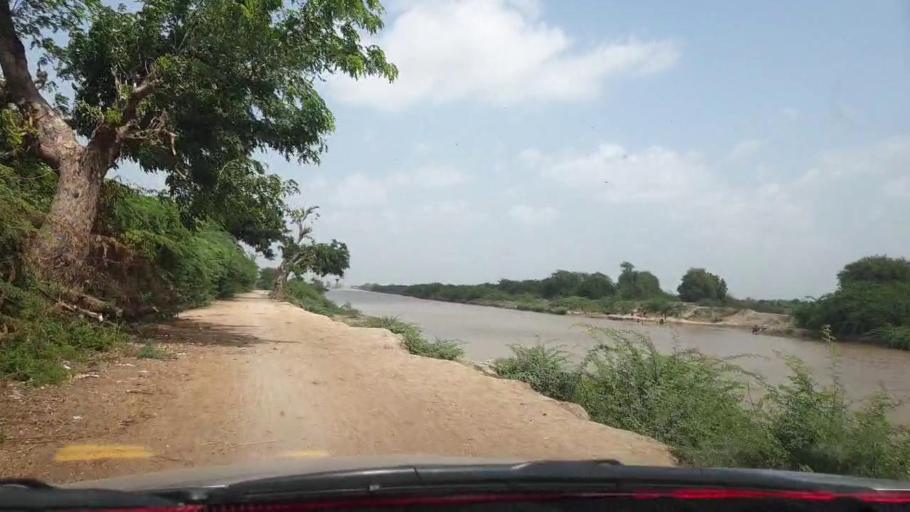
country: PK
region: Sindh
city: Talhar
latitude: 24.8877
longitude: 68.8349
